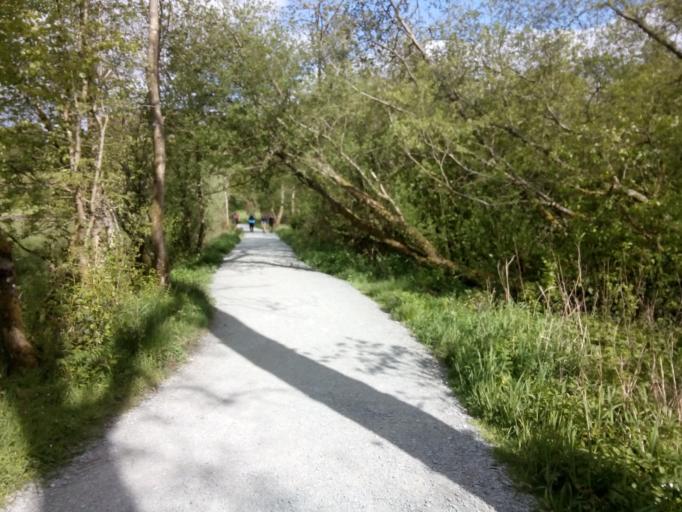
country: GB
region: England
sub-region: Cumbria
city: Ambleside
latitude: 54.4304
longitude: -3.0276
